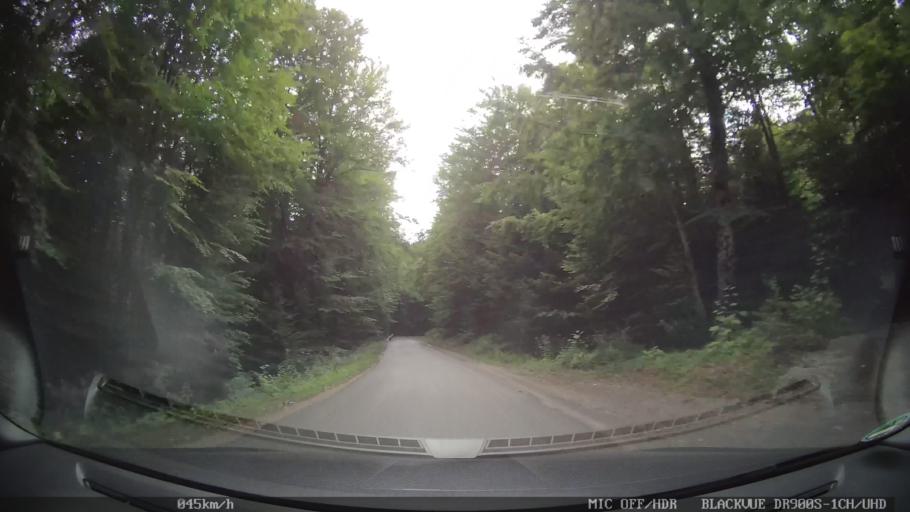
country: HR
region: Licko-Senjska
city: Jezerce
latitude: 44.9284
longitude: 15.5783
